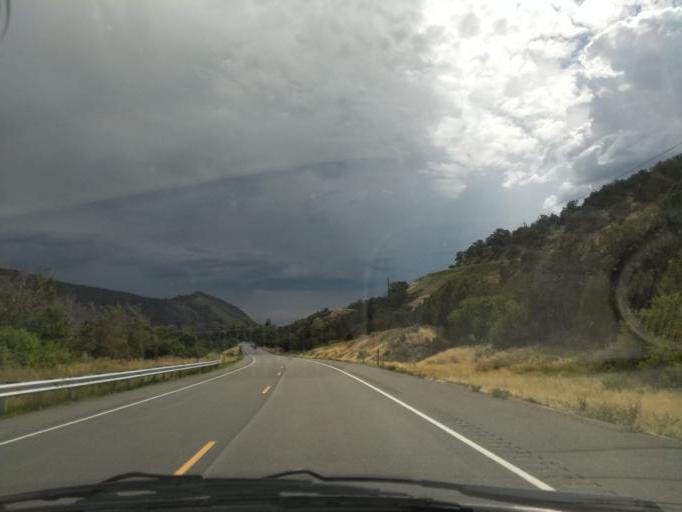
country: US
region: Colorado
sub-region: Delta County
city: Paonia
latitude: 38.9065
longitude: -107.5609
